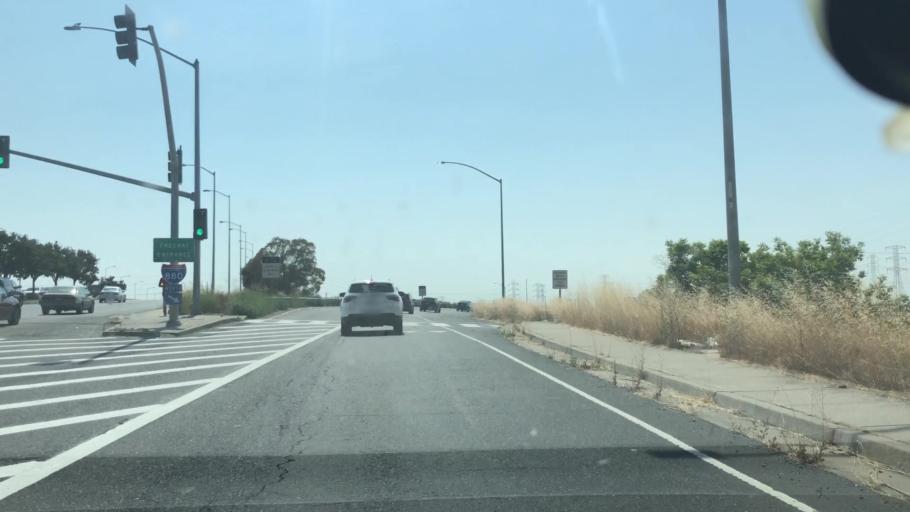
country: US
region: California
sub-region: Alameda County
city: Fremont
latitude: 37.5084
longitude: -121.9656
